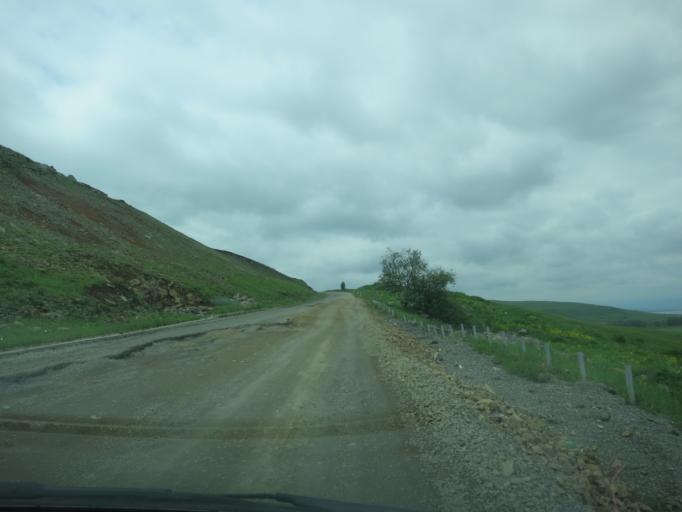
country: GE
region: Kvemo Kartli
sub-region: Tsalka
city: Tsalka
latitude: 41.6310
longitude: 44.1493
